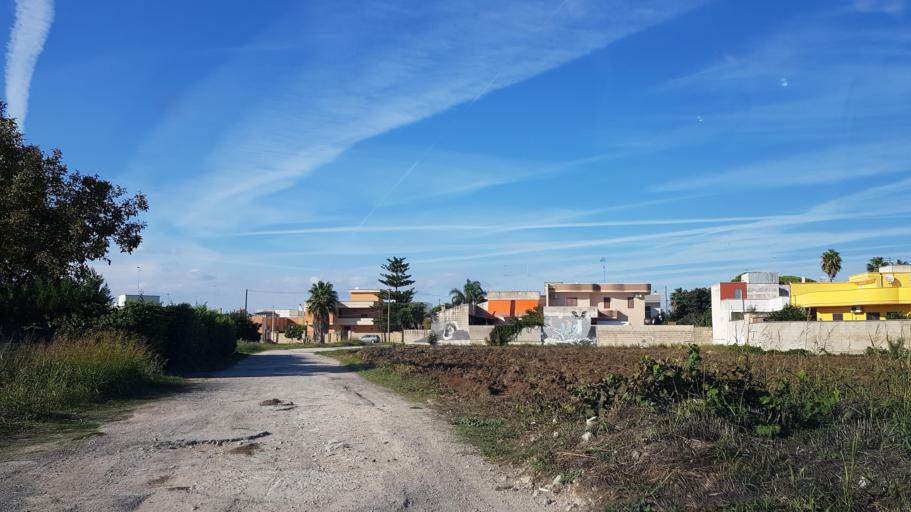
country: IT
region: Apulia
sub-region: Provincia di Lecce
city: Salice Salentino
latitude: 40.3855
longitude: 17.9569
